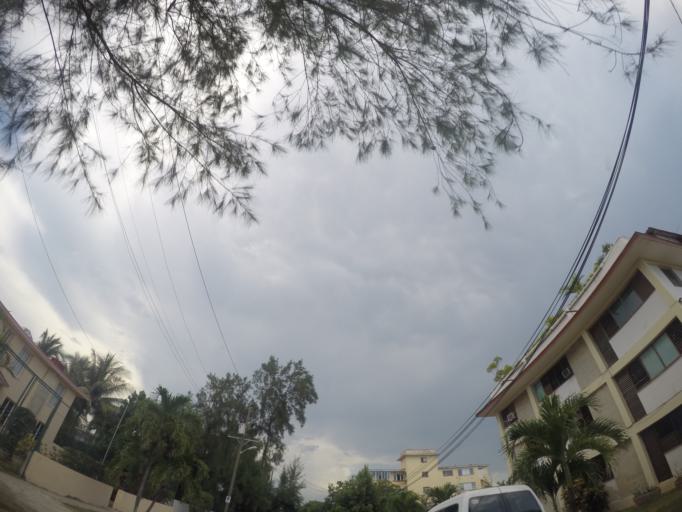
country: CU
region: La Habana
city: Havana
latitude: 23.1235
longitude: -82.4256
